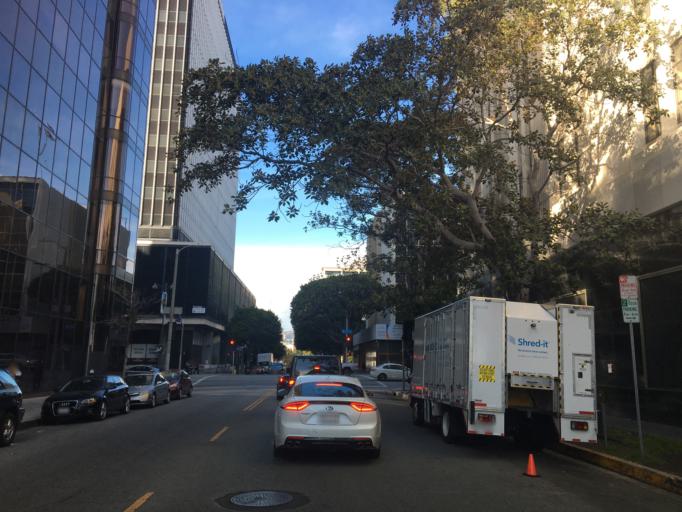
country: US
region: California
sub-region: Los Angeles County
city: Silver Lake
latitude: 34.0613
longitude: -118.2929
